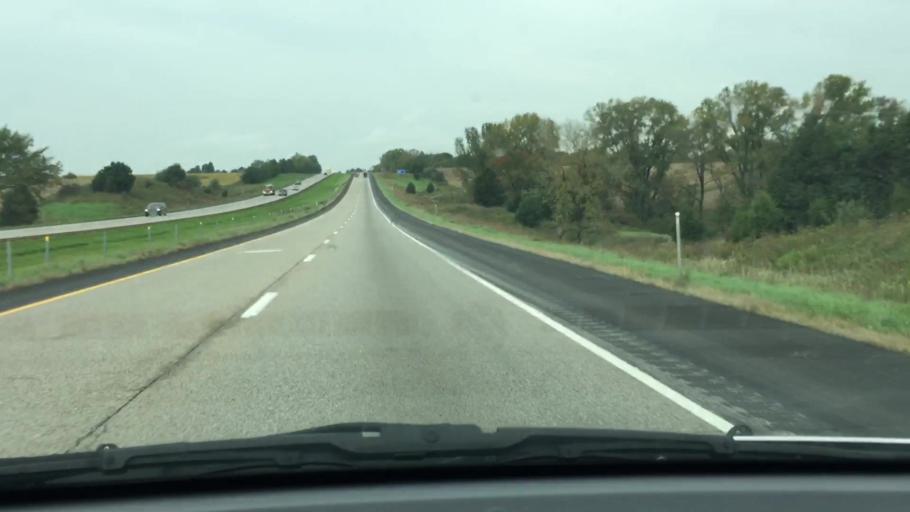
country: US
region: Iowa
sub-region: Muscatine County
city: West Liberty
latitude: 41.6529
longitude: -91.1842
